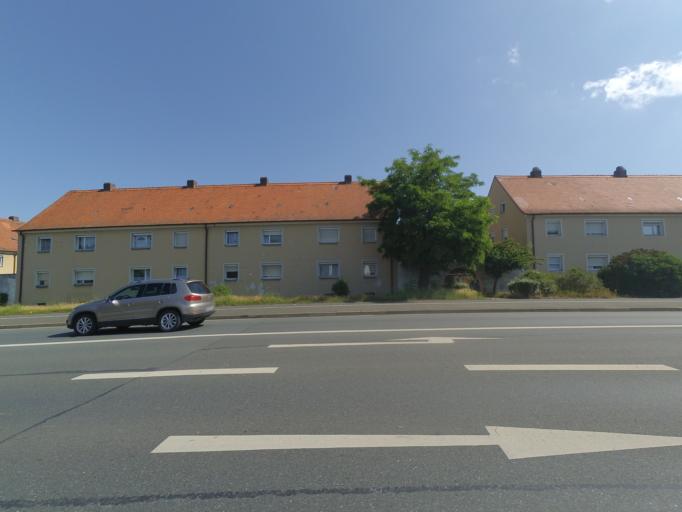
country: DE
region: Bavaria
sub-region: Regierungsbezirk Unterfranken
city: Kitzingen
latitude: 49.7315
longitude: 10.1809
